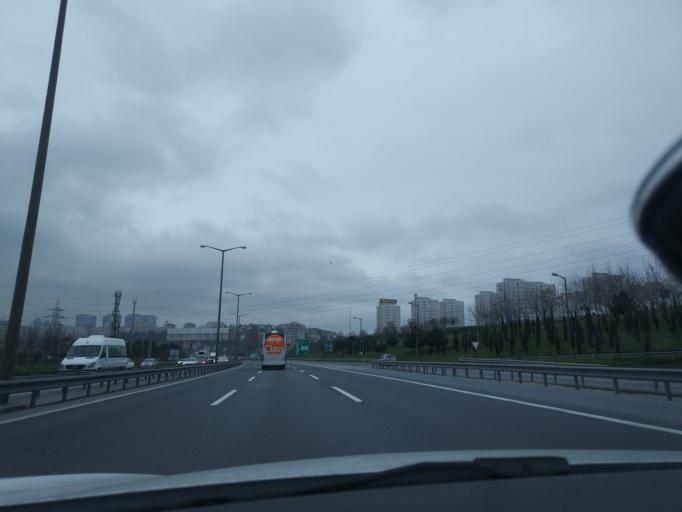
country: TR
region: Istanbul
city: Esenyurt
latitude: 41.0580
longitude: 28.7078
